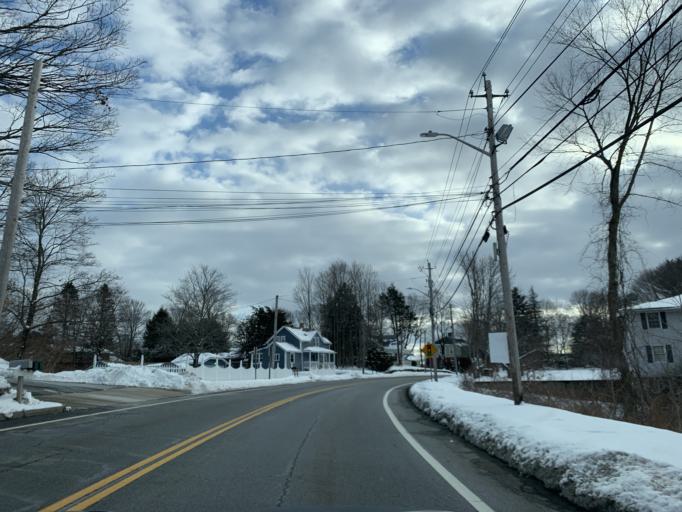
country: US
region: Rhode Island
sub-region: Providence County
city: Cumberland Hill
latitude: 41.9802
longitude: -71.4594
